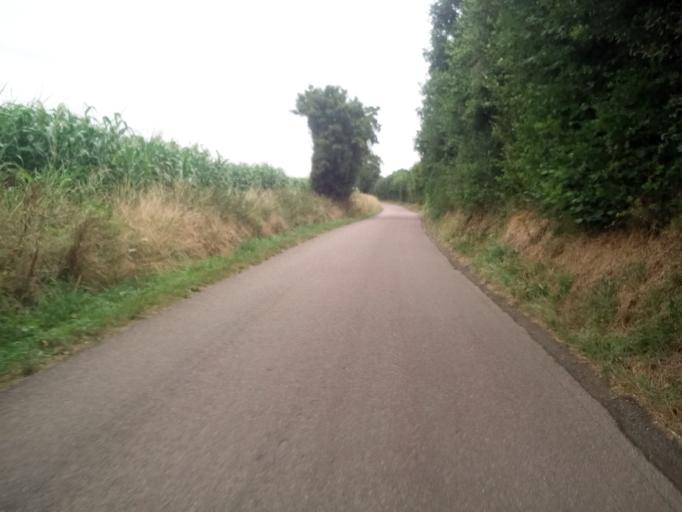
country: FR
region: Lower Normandy
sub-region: Departement du Calvados
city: Clinchamps-sur-Orne
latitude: 49.0368
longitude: -0.3934
